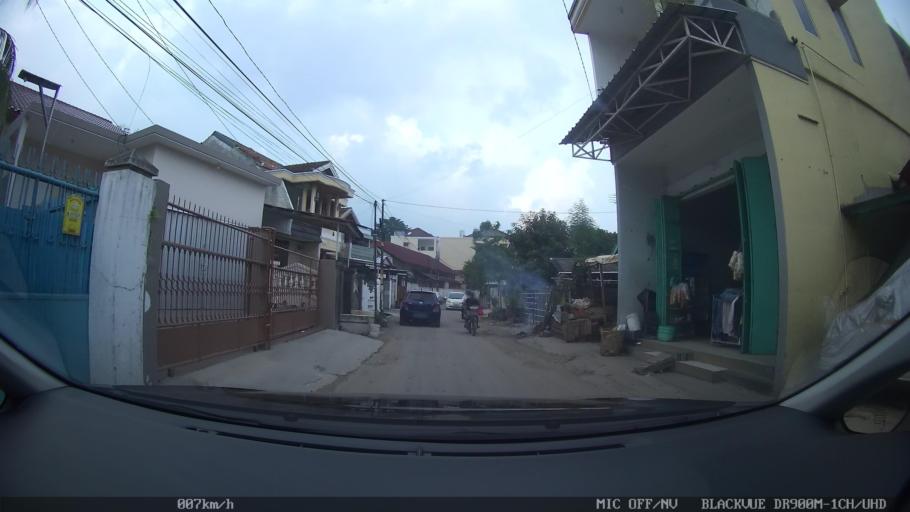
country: ID
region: Lampung
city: Bandarlampung
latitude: -5.4401
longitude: 105.2835
